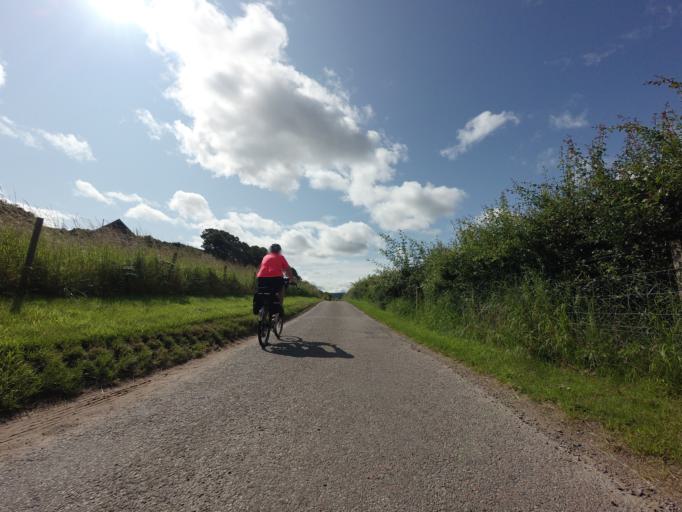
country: GB
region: Scotland
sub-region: Moray
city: Kinloss
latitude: 57.6406
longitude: -3.5215
